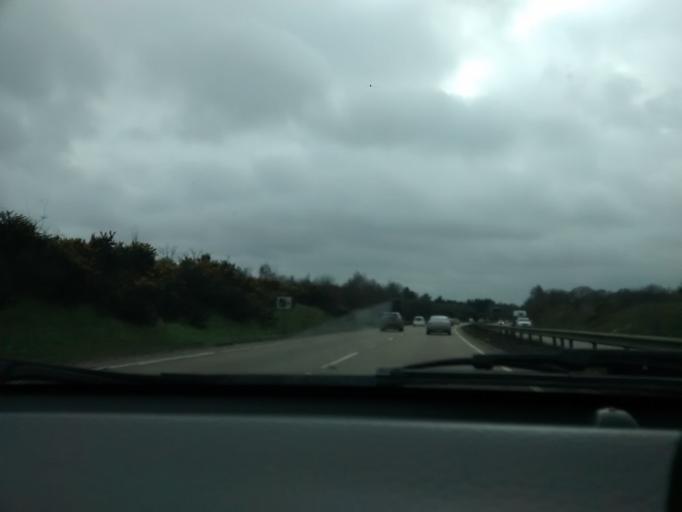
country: GB
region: England
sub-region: Suffolk
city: Kesgrave
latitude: 52.0239
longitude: 1.1988
